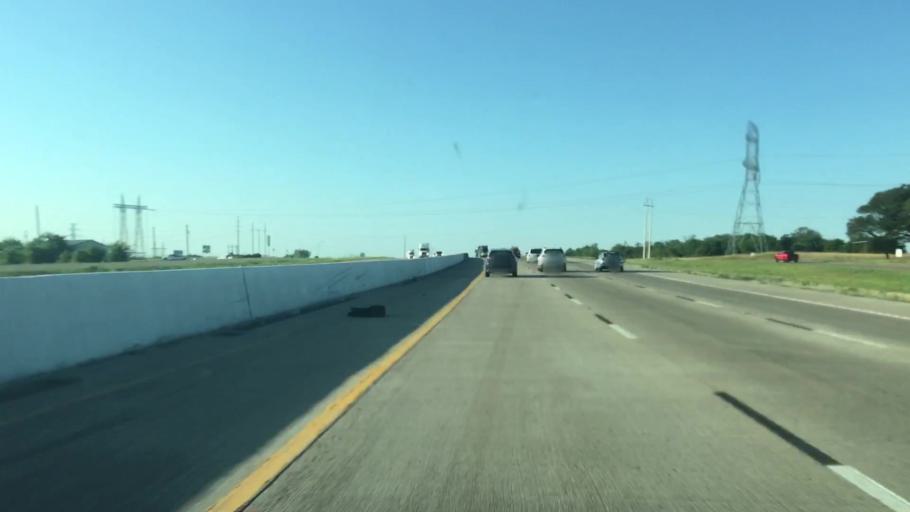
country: US
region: Texas
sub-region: McLennan County
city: Northcrest
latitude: 31.7034
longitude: -97.1024
